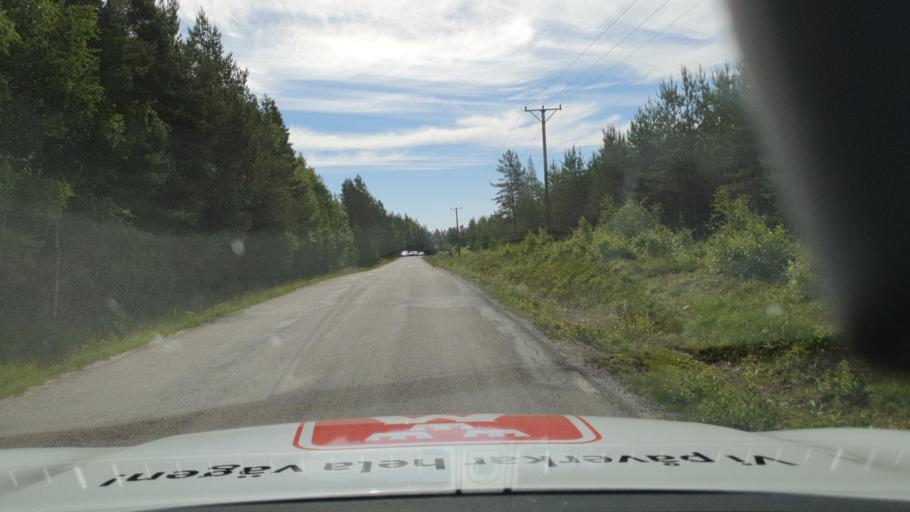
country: SE
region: Vaesterbotten
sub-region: Umea Kommun
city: Saevar
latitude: 63.8680
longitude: 20.7305
